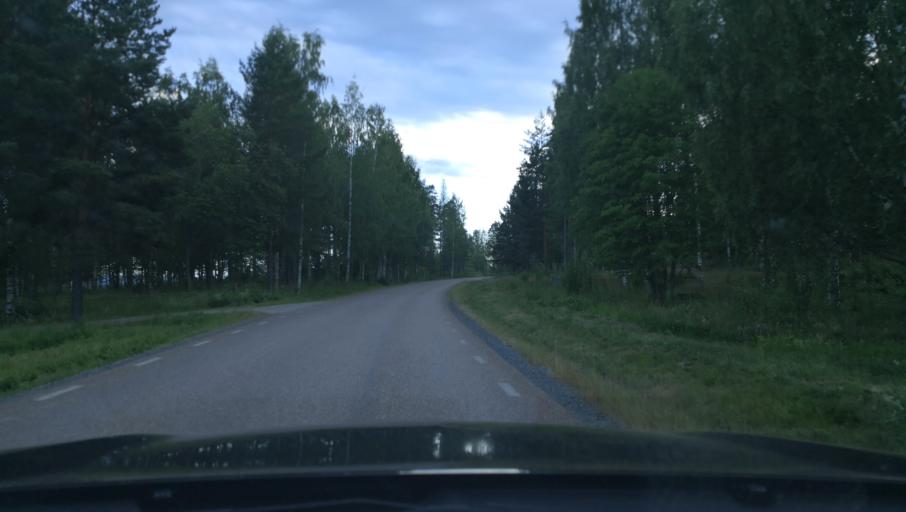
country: SE
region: Dalarna
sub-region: Ludvika Kommun
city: Ludvika
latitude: 60.1185
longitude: 15.2605
